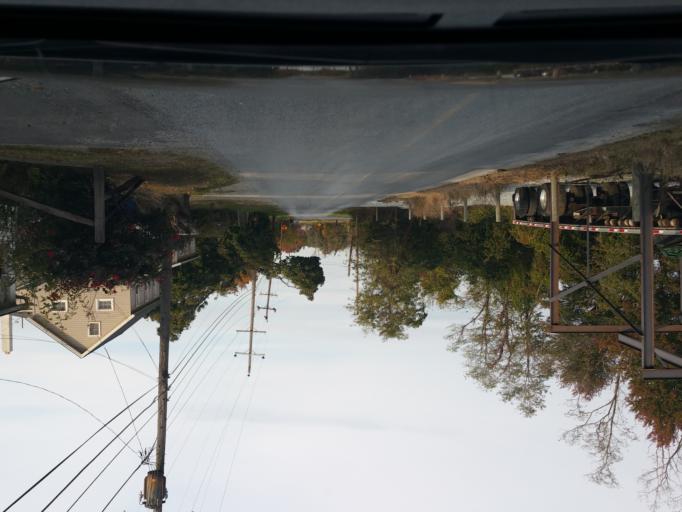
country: US
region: Maryland
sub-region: Cecil County
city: Rising Sun
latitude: 39.7222
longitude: -76.0278
